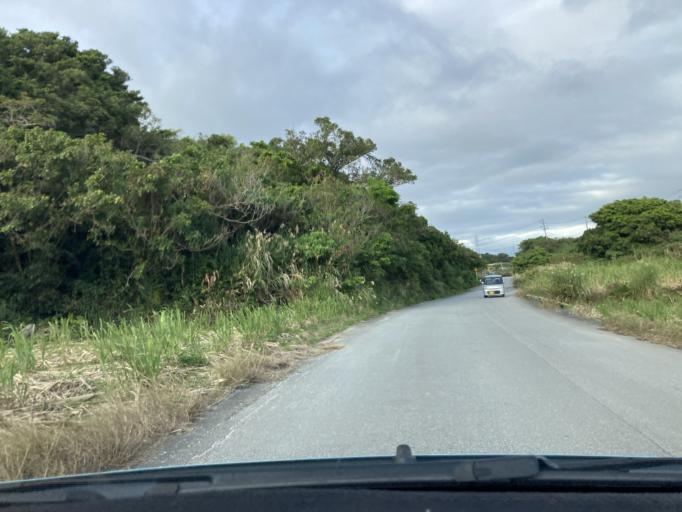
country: JP
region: Okinawa
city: Itoman
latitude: 26.1155
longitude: 127.6810
